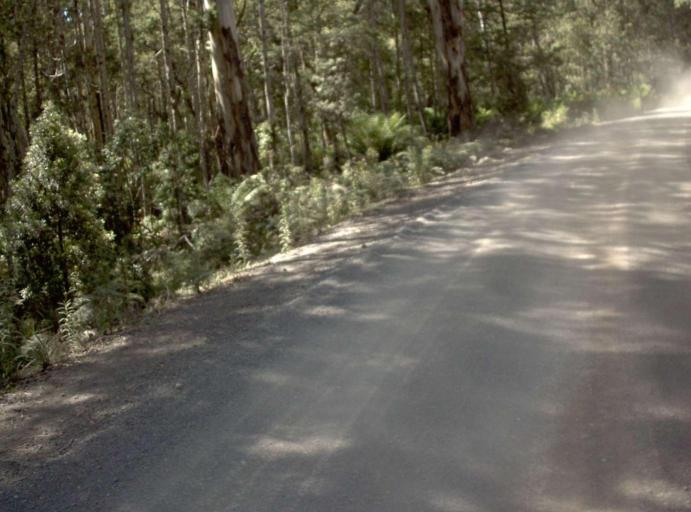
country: AU
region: New South Wales
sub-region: Bombala
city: Bombala
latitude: -37.2313
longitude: 148.7532
